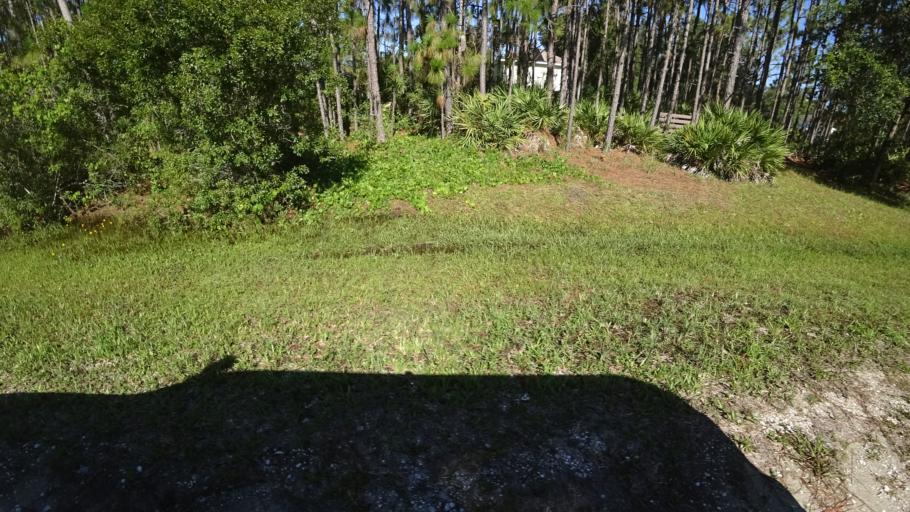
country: US
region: Florida
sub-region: Sarasota County
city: Fruitville
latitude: 27.4000
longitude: -82.2999
